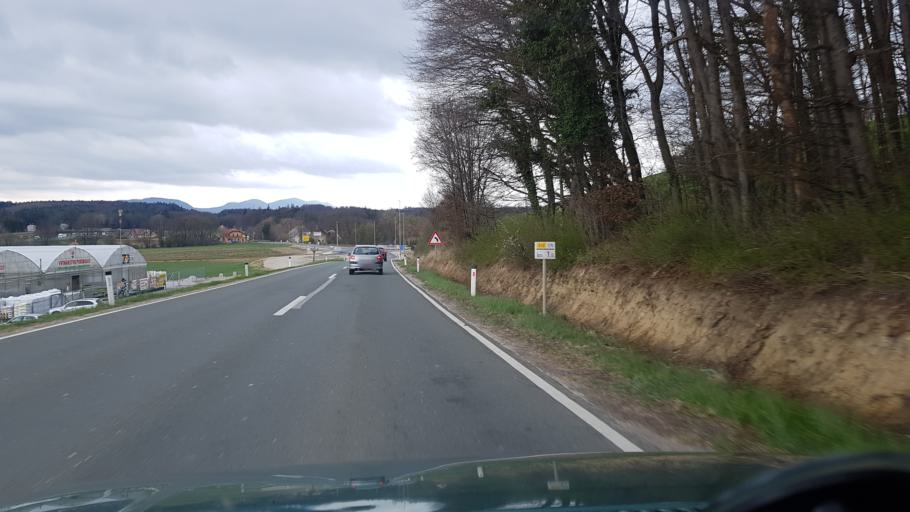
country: SI
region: Slovenska Bistrica
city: Slovenska Bistrica
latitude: 46.3780
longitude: 15.5544
